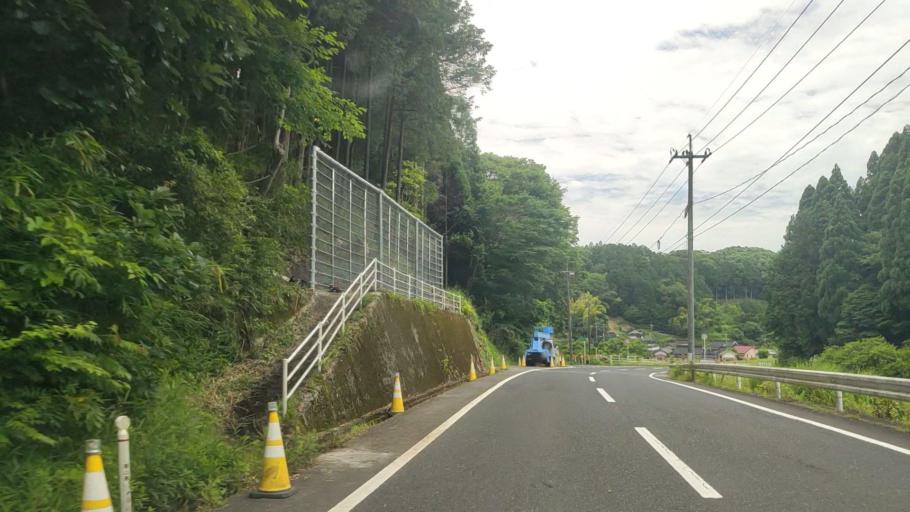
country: JP
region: Okayama
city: Tsuyama
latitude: 35.0977
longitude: 134.2806
